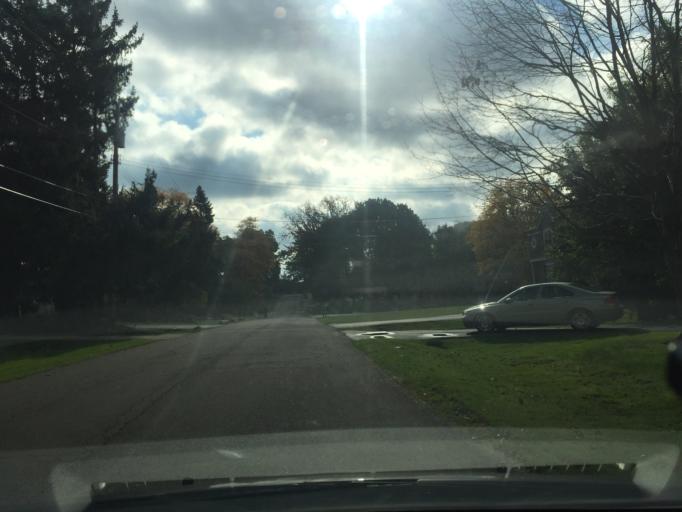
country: US
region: Michigan
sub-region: Oakland County
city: Sylvan Lake
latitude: 42.5944
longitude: -83.3210
